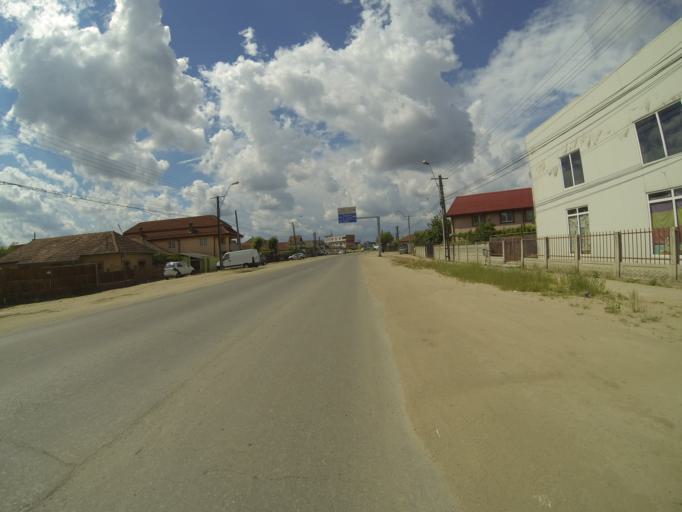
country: RO
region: Dolj
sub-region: Municipiul Craiova
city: Popoveni
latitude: 44.2850
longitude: 23.8009
